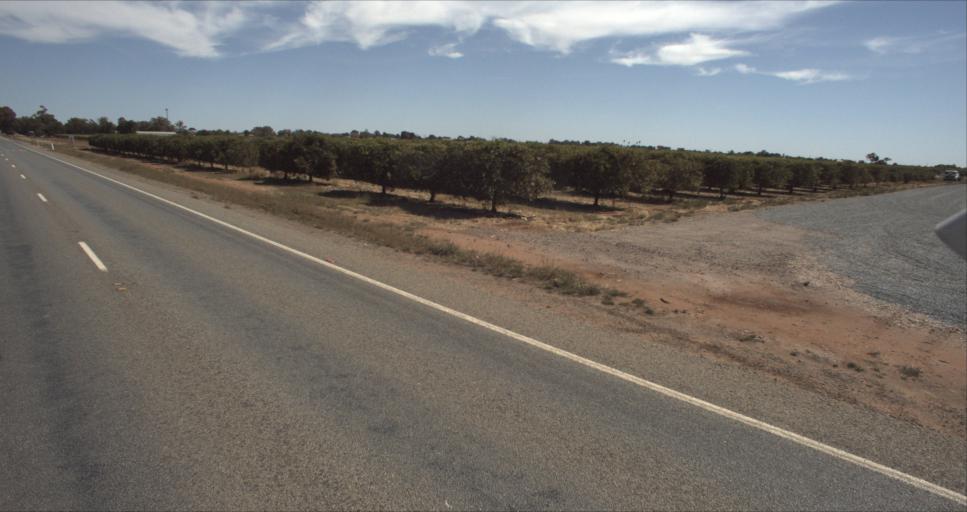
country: AU
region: New South Wales
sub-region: Leeton
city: Leeton
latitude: -34.5835
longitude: 146.4151
